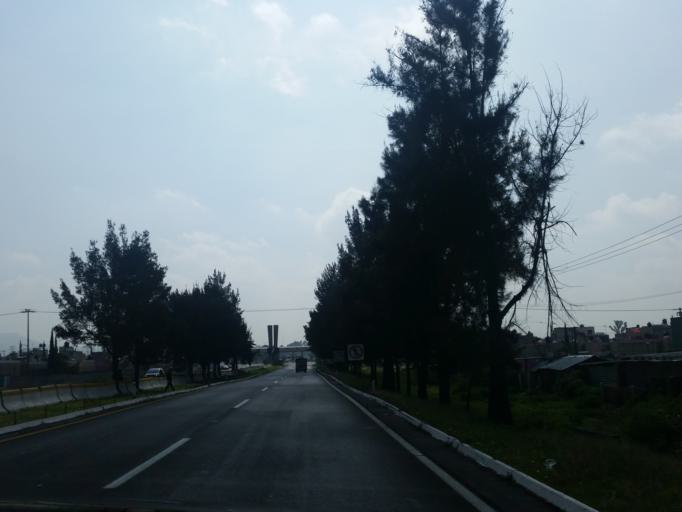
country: MX
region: Mexico
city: Santo Tomas Chiconautla
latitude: 19.6108
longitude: -99.0293
